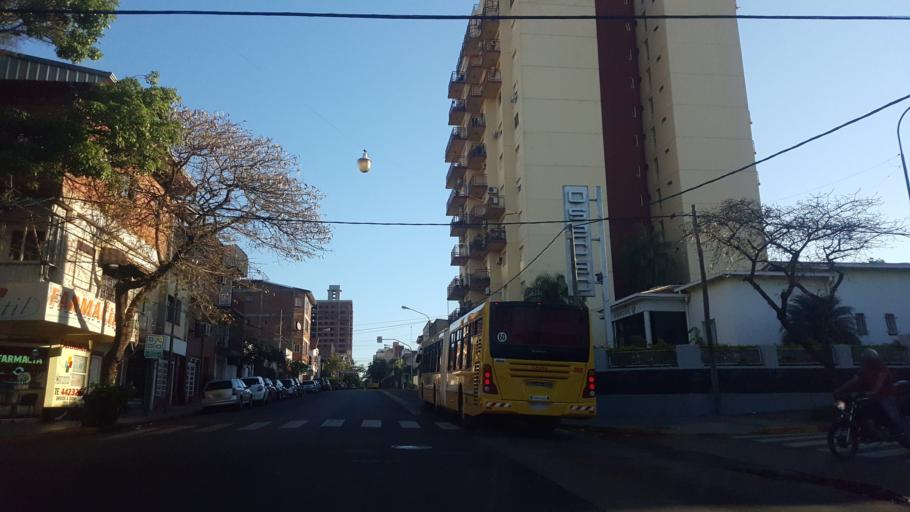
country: AR
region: Misiones
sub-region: Departamento de Capital
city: Posadas
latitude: -27.3617
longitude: -55.8971
